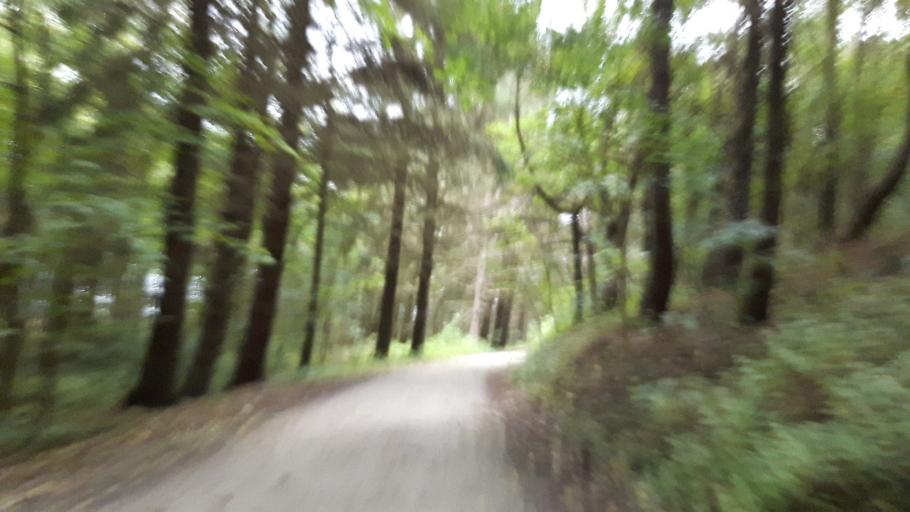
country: NL
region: Friesland
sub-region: Gemeente Ameland
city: Nes
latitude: 53.4538
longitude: 5.7568
